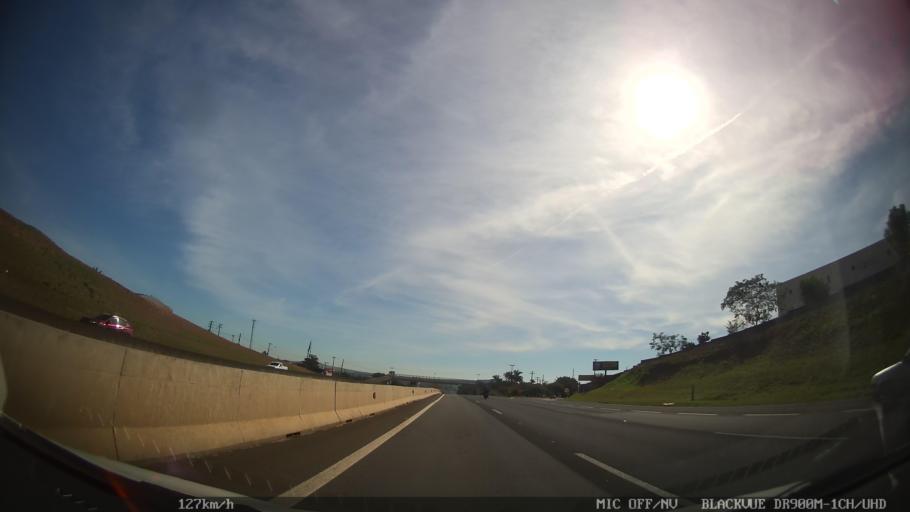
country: BR
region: Sao Paulo
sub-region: Araras
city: Araras
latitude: -22.3762
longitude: -47.3943
